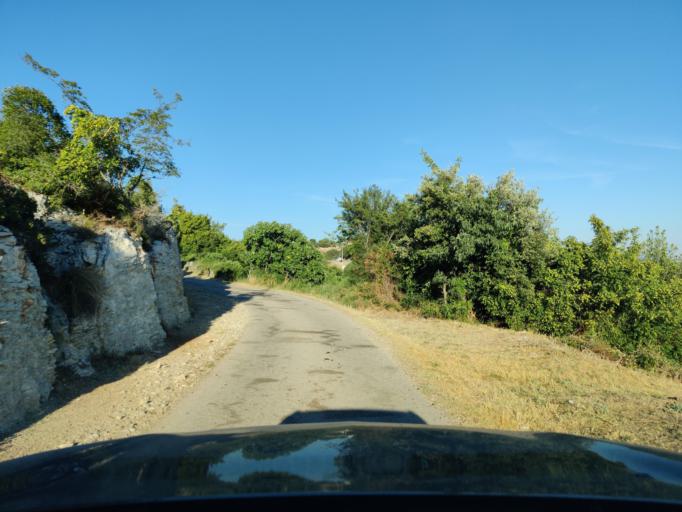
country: HR
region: Sibensko-Kniniska
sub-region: Grad Sibenik
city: Pirovac
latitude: 43.8640
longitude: 15.7144
